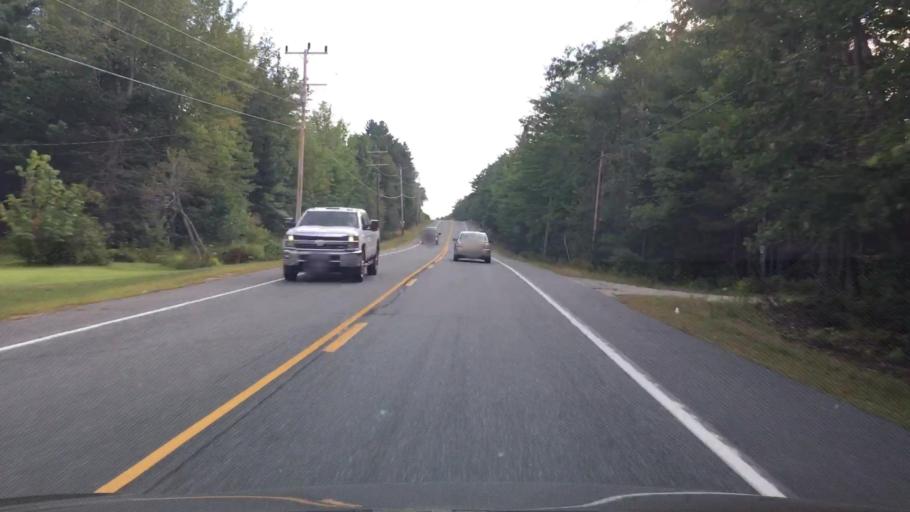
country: US
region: Maine
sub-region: Hancock County
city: Surry
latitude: 44.4537
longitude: -68.5538
